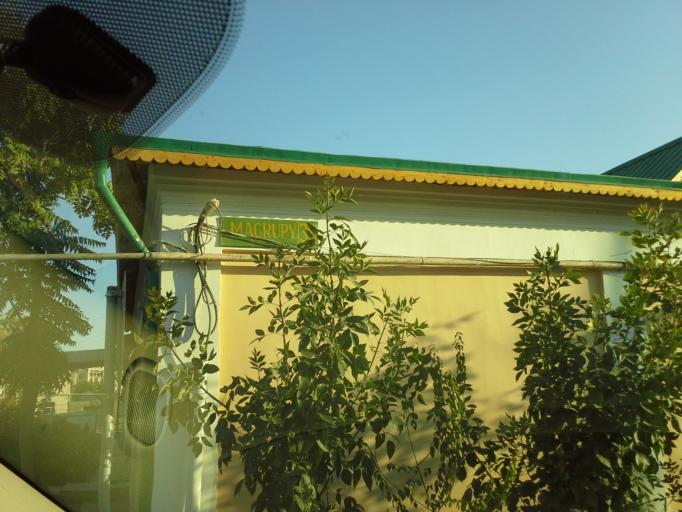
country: TM
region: Dasoguz
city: Dasoguz
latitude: 41.8208
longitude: 59.9799
